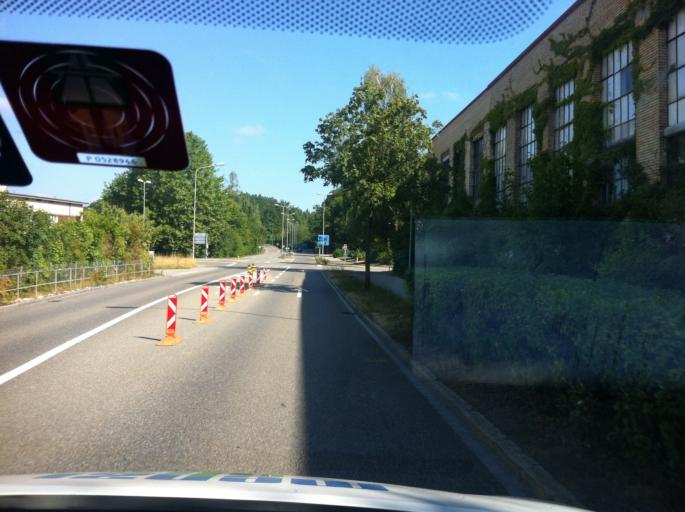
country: CH
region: Zurich
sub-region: Bezirk Buelach
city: Buelach / Soligaenter
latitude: 47.5267
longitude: 8.5358
